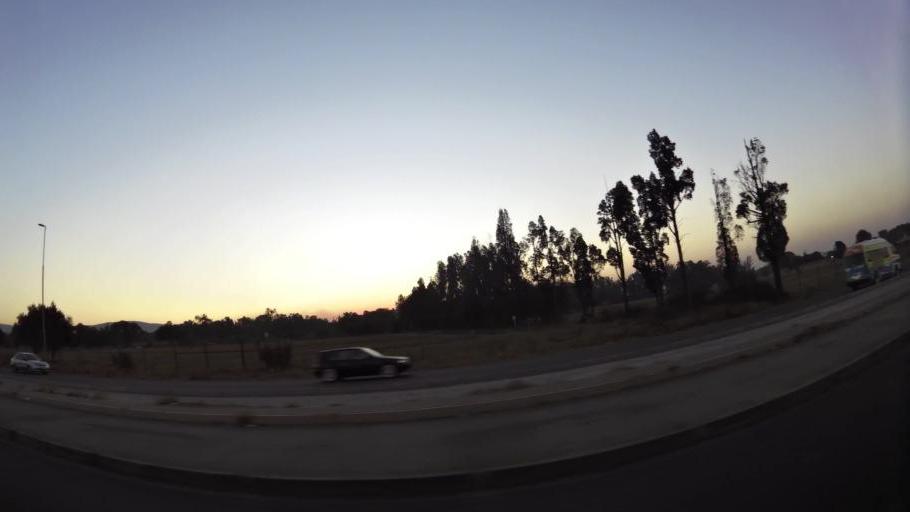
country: ZA
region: North-West
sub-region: Bojanala Platinum District Municipality
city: Rustenburg
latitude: -25.6423
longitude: 27.2621
